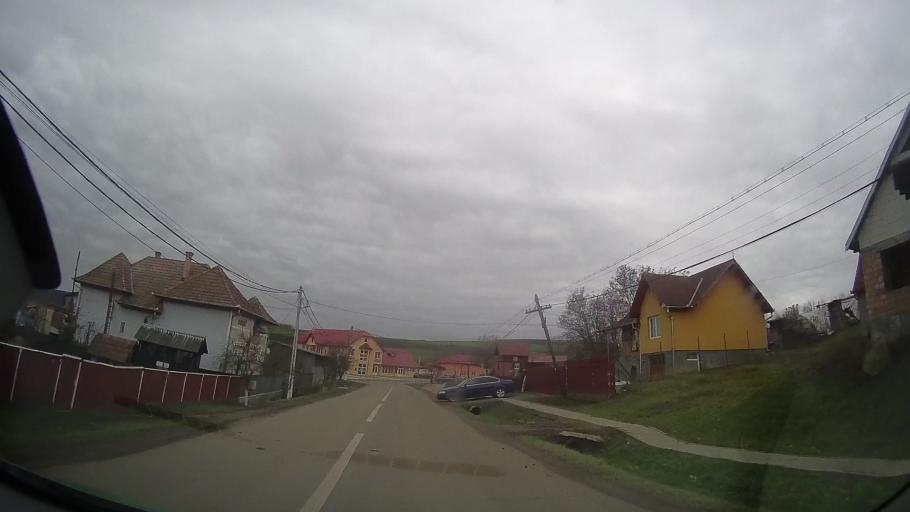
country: RO
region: Mures
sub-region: Comuna Craesti
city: Craiesti
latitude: 46.7561
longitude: 24.4219
